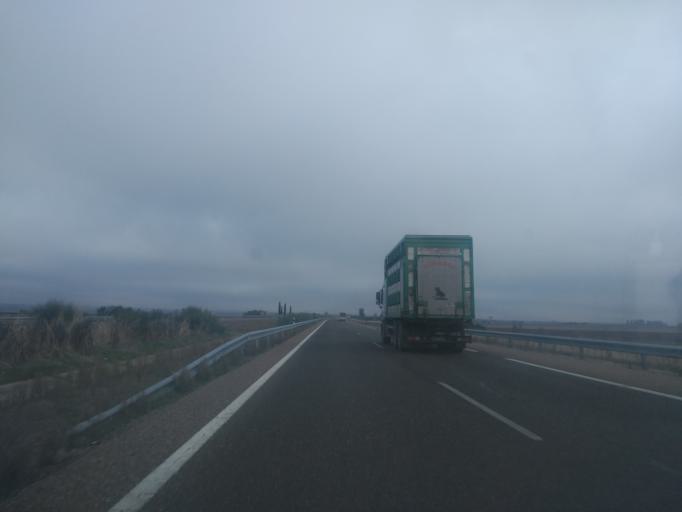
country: ES
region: Castille and Leon
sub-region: Provincia de Salamanca
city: Gomecello
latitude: 41.0410
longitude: -5.5602
